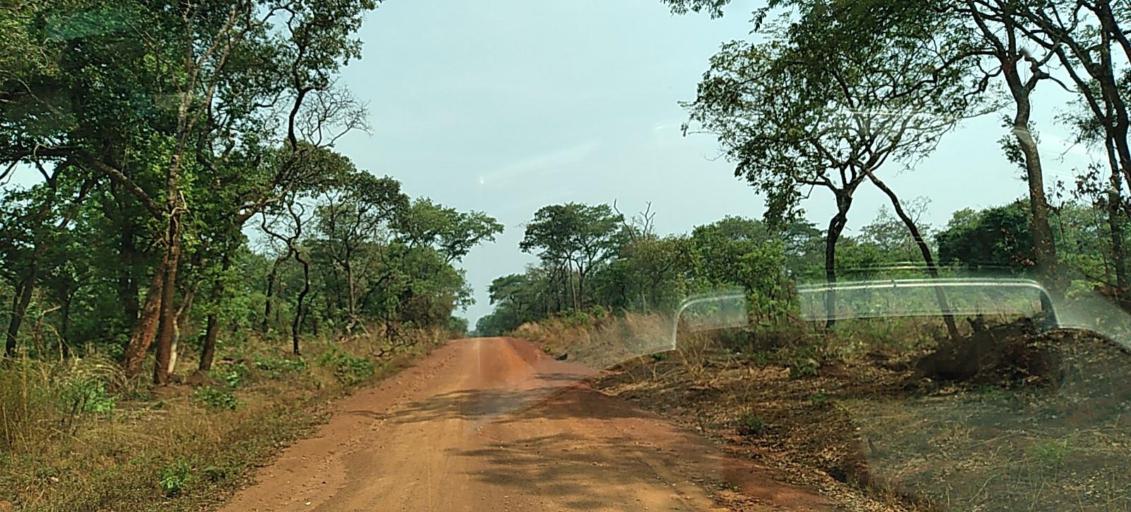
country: ZM
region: North-Western
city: Kansanshi
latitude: -11.9954
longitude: 26.8379
